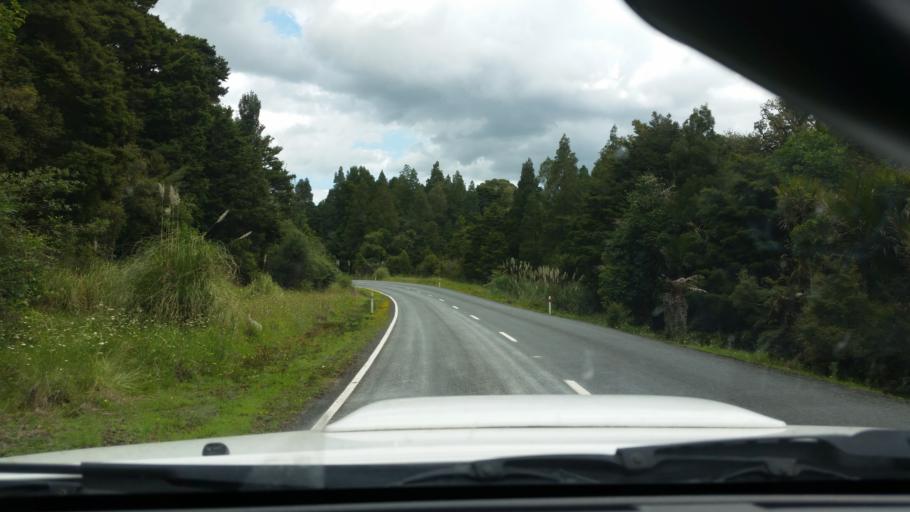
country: NZ
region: Northland
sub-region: Kaipara District
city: Dargaville
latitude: -35.7745
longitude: 173.9077
